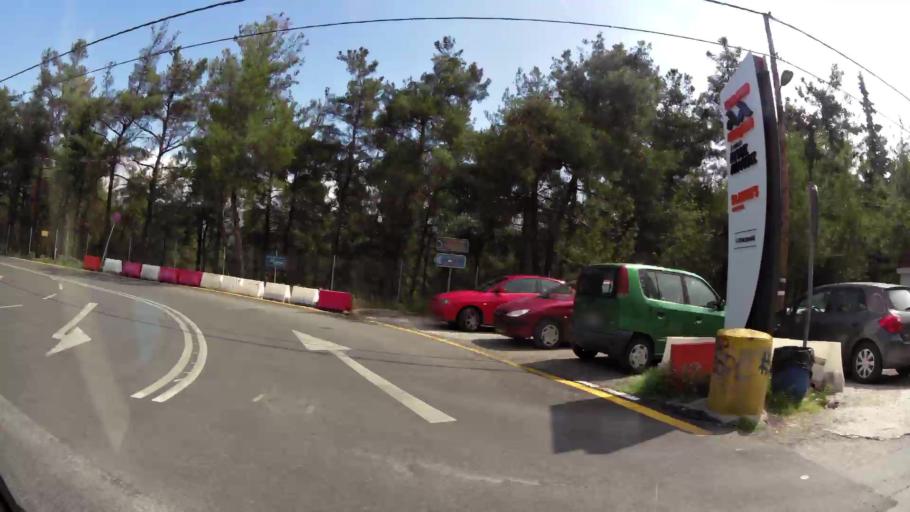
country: GR
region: Central Macedonia
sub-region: Nomos Thessalonikis
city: Panorama
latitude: 40.5927
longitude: 23.0165
